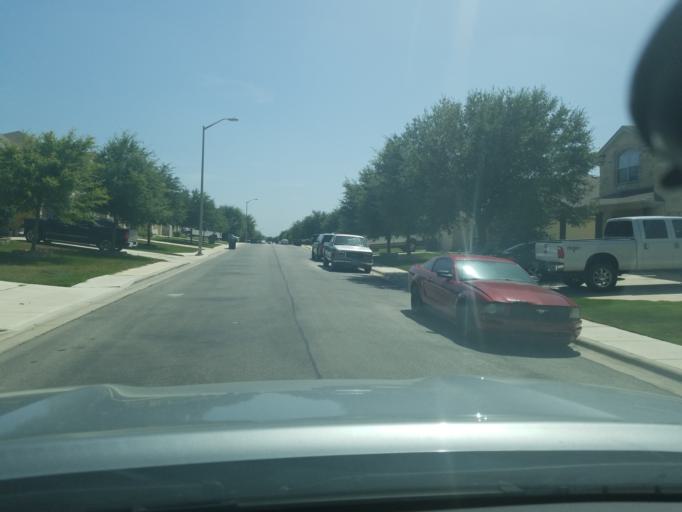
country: US
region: Texas
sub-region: Guadalupe County
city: Lake Dunlap
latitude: 29.6763
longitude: -98.0363
